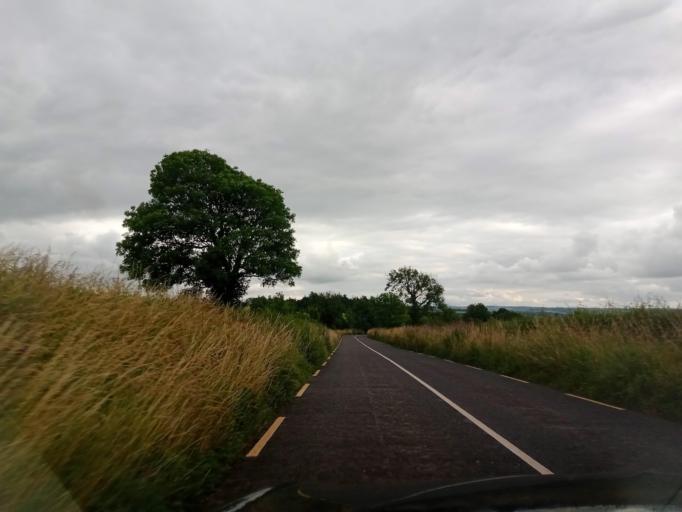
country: IE
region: Leinster
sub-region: Kilkenny
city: Castlecomer
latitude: 52.9039
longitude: -7.1798
